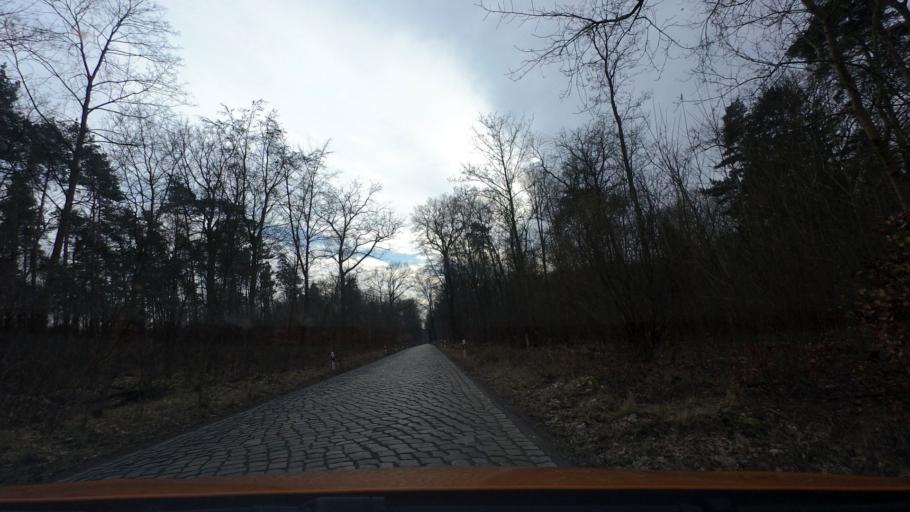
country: DE
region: Berlin
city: Buch
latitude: 52.6539
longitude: 13.4862
